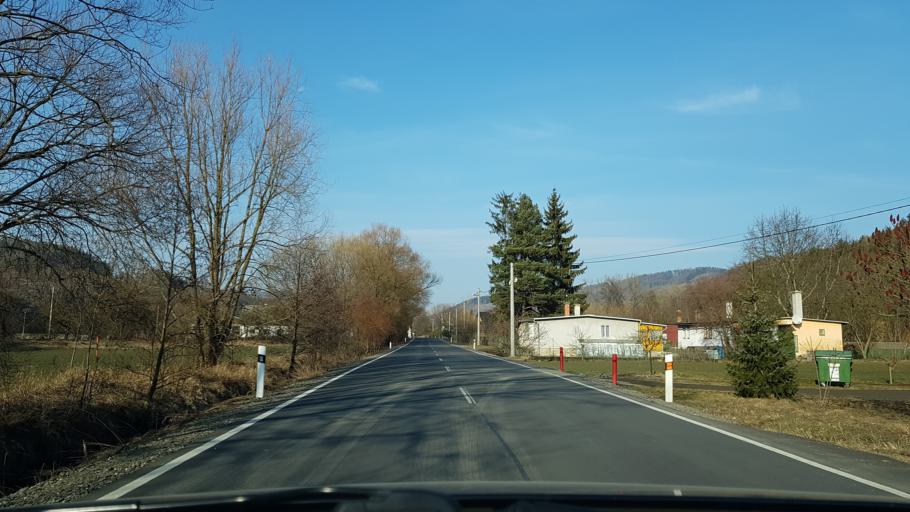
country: CZ
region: Olomoucky
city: Dolni Bohdikov
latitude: 49.9941
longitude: 16.8932
